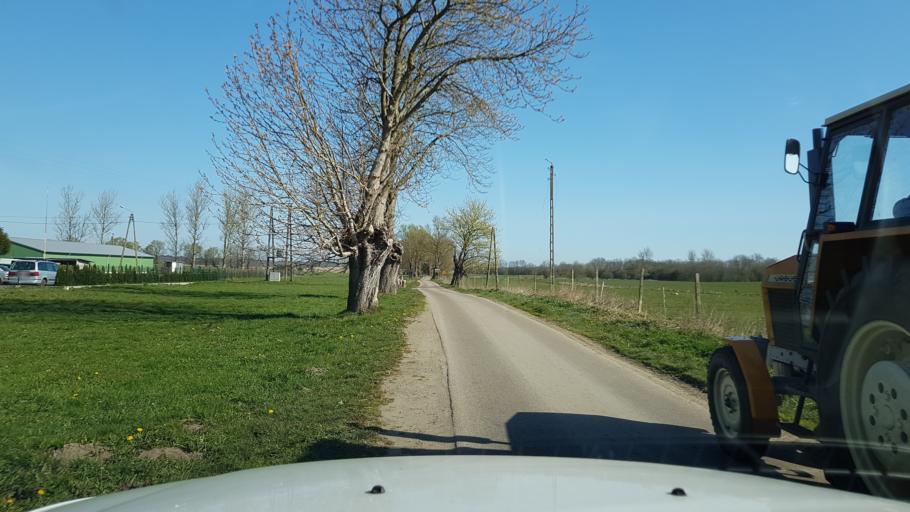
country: PL
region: West Pomeranian Voivodeship
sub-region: Powiat kolobrzeski
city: Ustronie Morskie
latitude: 54.2160
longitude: 15.8481
